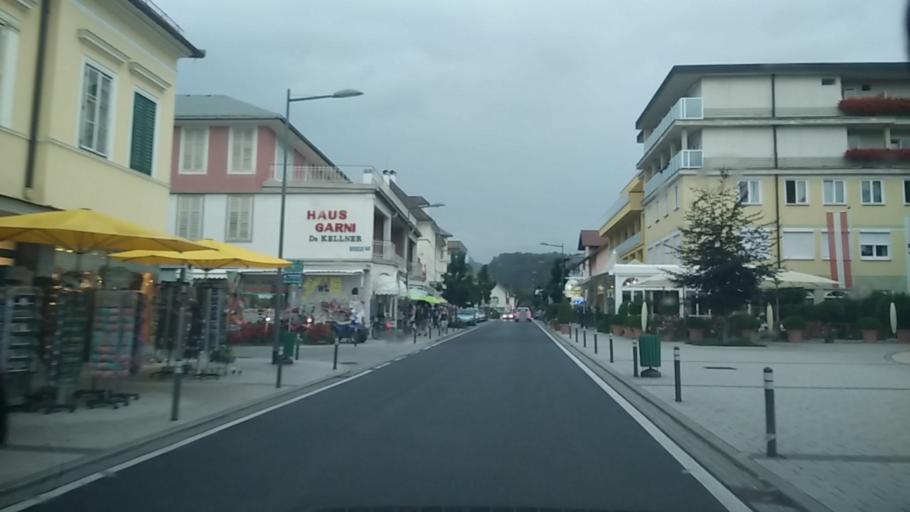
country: AT
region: Carinthia
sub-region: Politischer Bezirk Klagenfurt Land
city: Maria Worth
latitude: 46.6357
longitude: 14.1439
